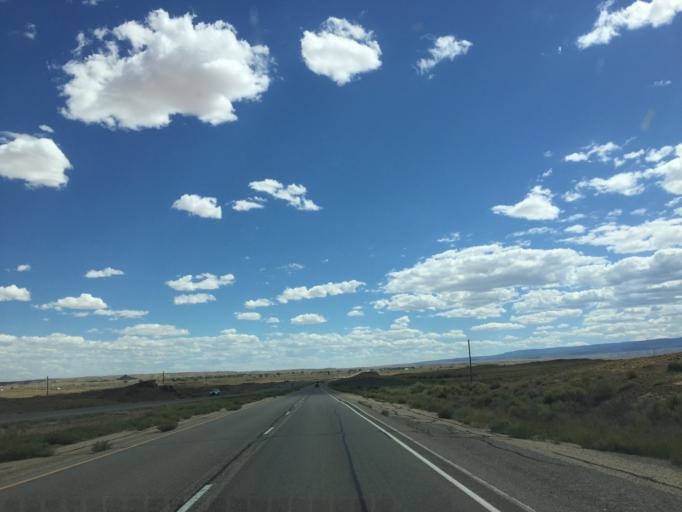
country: US
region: New Mexico
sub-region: San Juan County
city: Shiprock
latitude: 36.3266
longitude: -108.7104
